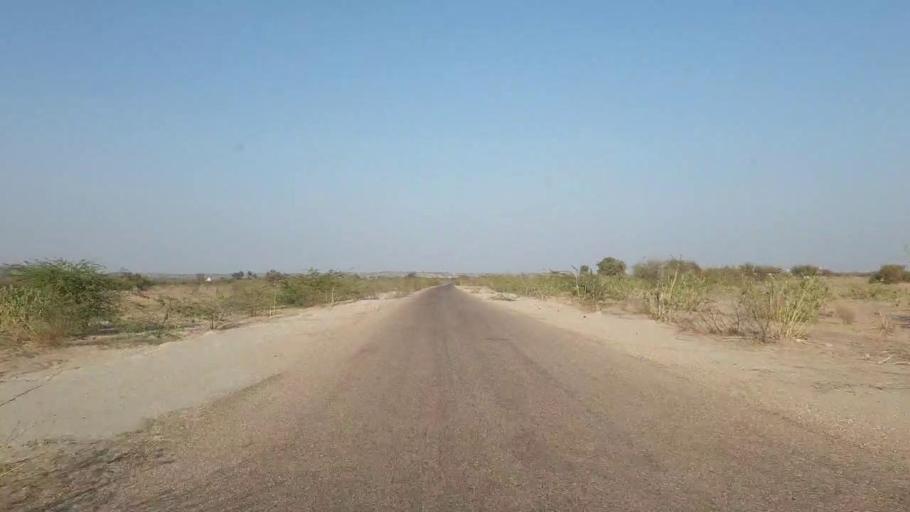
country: PK
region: Sindh
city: Chor
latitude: 25.5817
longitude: 69.8220
